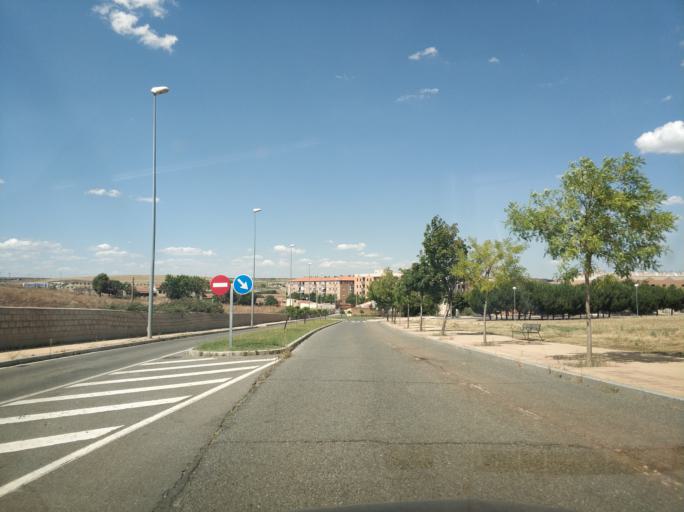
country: ES
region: Castille and Leon
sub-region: Provincia de Salamanca
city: Aldeatejada
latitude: 40.9498
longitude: -5.6945
